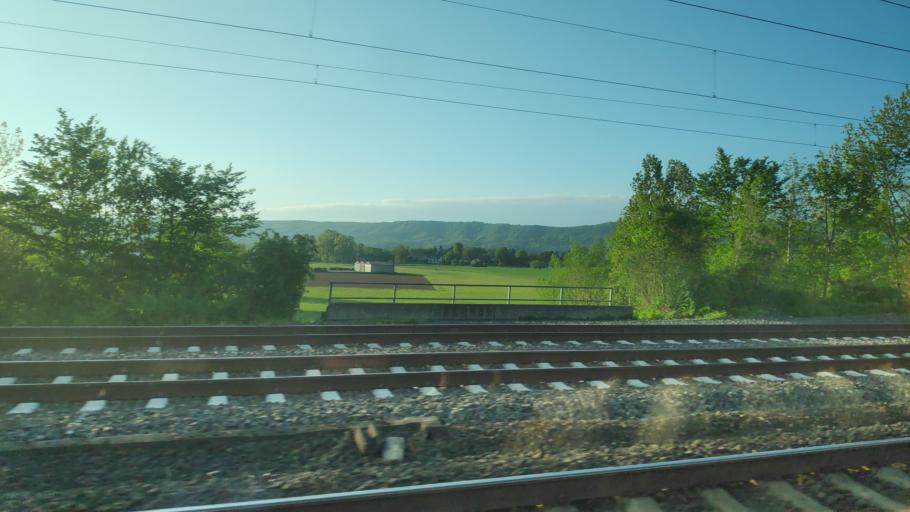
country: DE
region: North Rhine-Westphalia
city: Porta Westfalica
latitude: 52.2196
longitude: 8.8691
